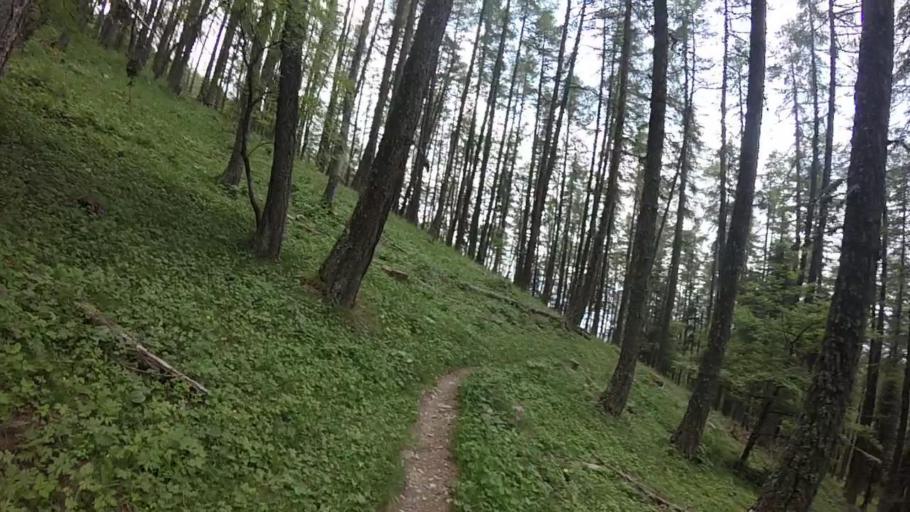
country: FR
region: Provence-Alpes-Cote d'Azur
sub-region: Departement des Alpes-de-Haute-Provence
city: Seyne-les-Alpes
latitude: 44.4110
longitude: 6.3730
